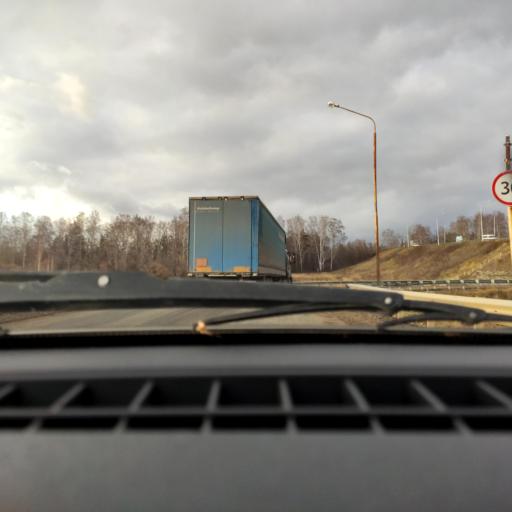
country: RU
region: Bashkortostan
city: Iglino
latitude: 54.7715
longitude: 56.2574
